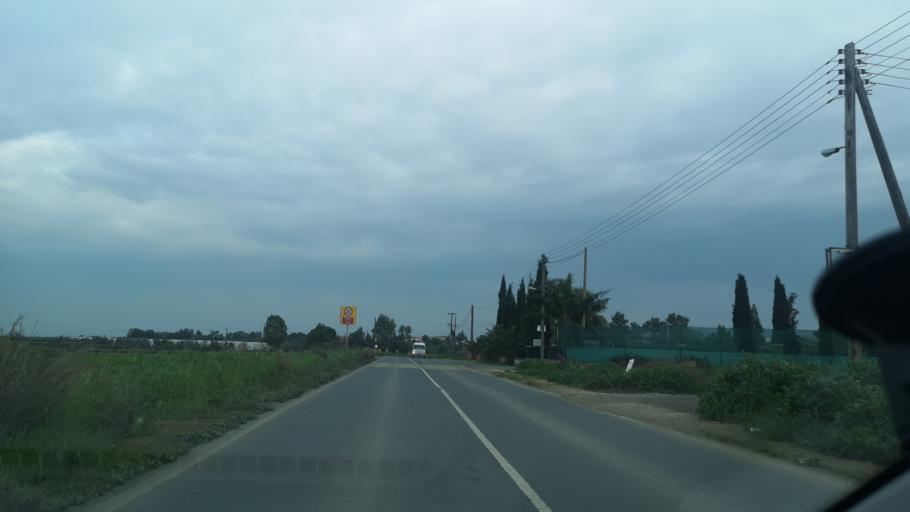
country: CY
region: Lefkosia
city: Kato Deftera
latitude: 35.0842
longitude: 33.2940
